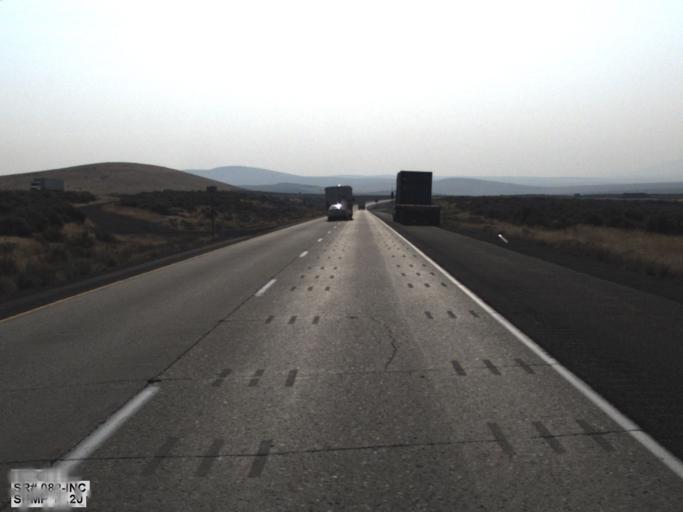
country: US
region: Washington
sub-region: Kittitas County
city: Kittitas
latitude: 46.8468
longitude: -120.3855
